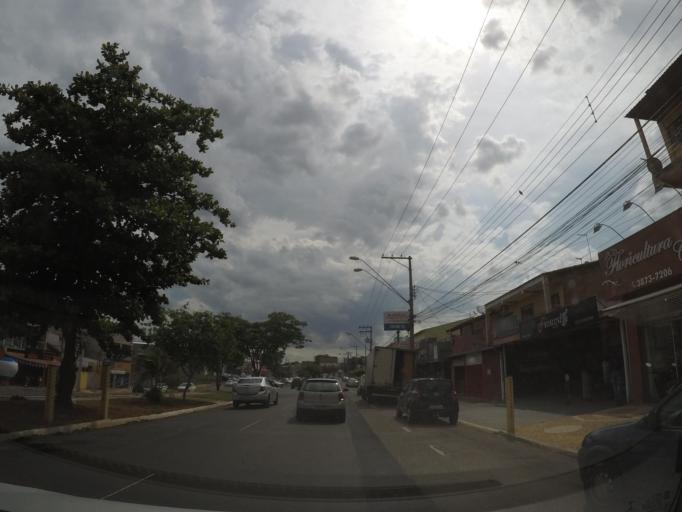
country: BR
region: Sao Paulo
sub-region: Sumare
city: Sumare
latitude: -22.8118
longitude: -47.2334
